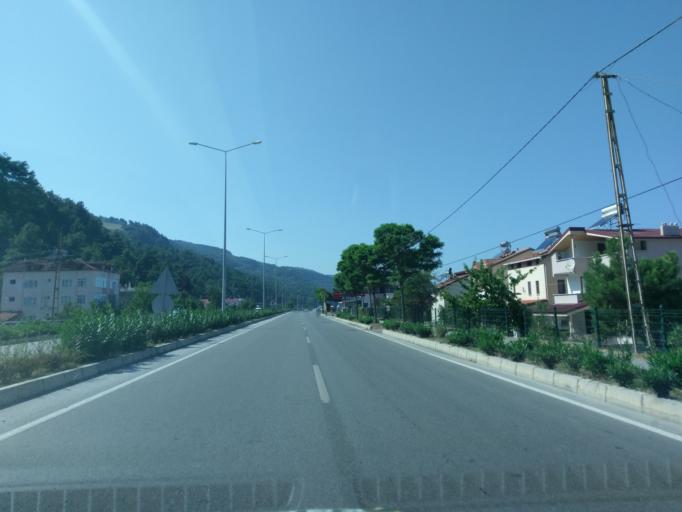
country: TR
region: Samsun
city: Yakakent
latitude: 41.6436
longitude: 35.4833
